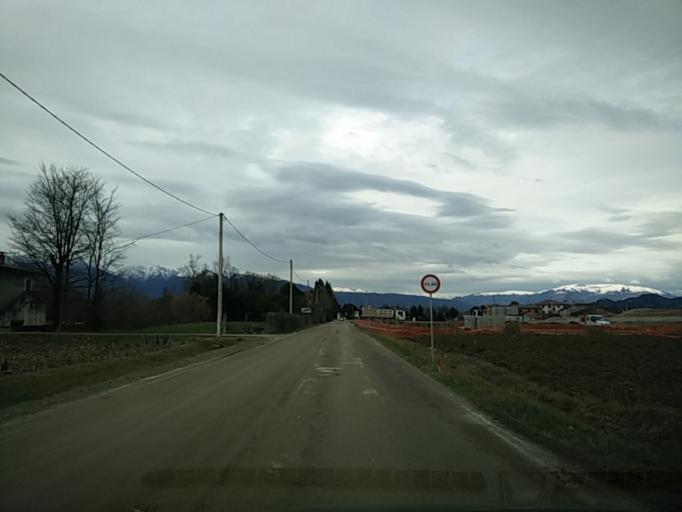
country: IT
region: Veneto
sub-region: Provincia di Treviso
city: Villa d'Asolo
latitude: 45.7540
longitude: 11.8793
